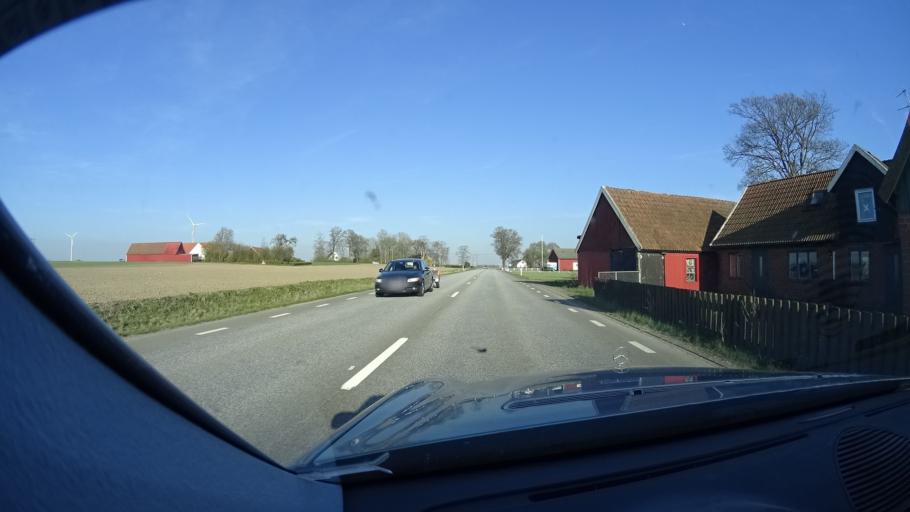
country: SE
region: Skane
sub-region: Svalovs Kommun
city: Teckomatorp
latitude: 55.8719
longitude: 13.1134
